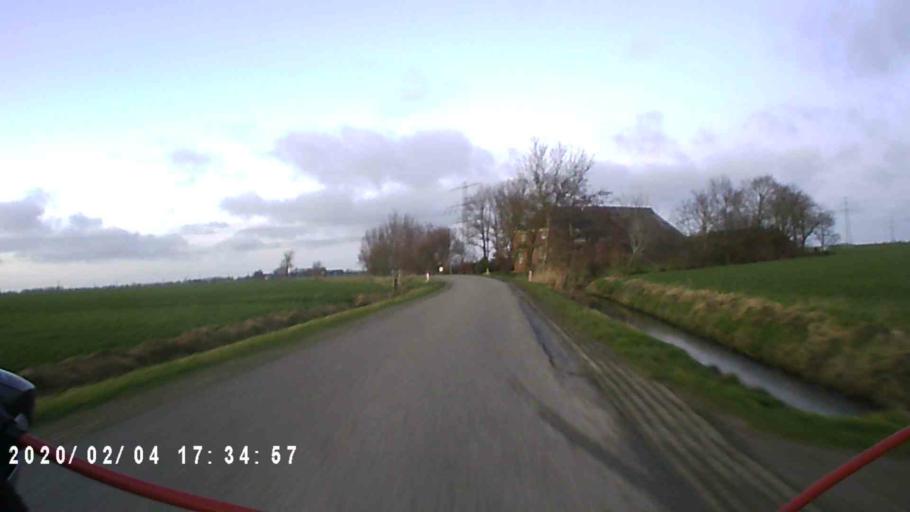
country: NL
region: Groningen
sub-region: Gemeente Zuidhorn
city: Aduard
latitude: 53.2875
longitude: 6.4937
